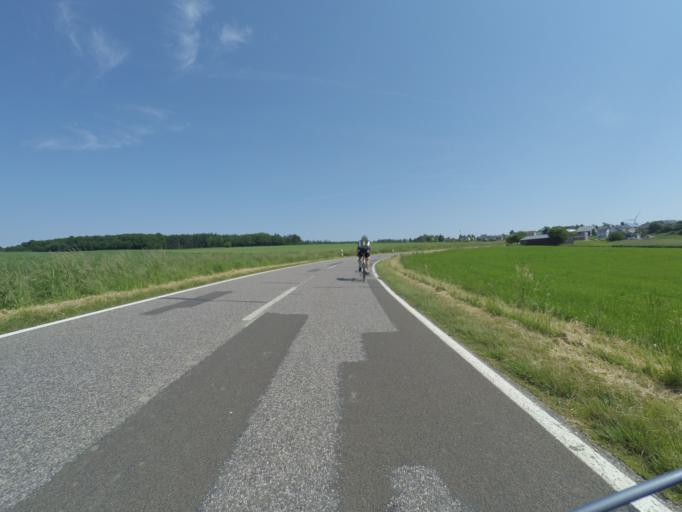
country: DE
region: Rheinland-Pfalz
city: Spesenroth
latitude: 50.0476
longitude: 7.4534
